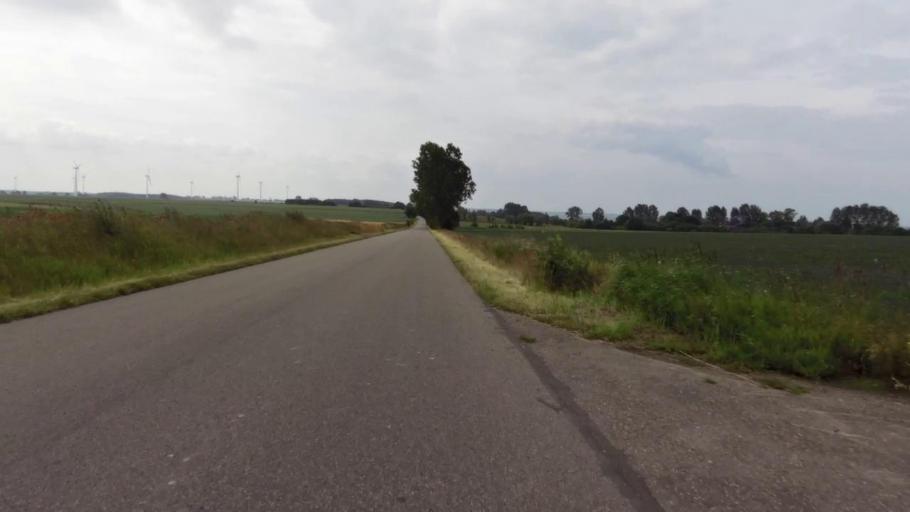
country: PL
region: West Pomeranian Voivodeship
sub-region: Powiat kamienski
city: Wolin
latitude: 53.8191
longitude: 14.6149
